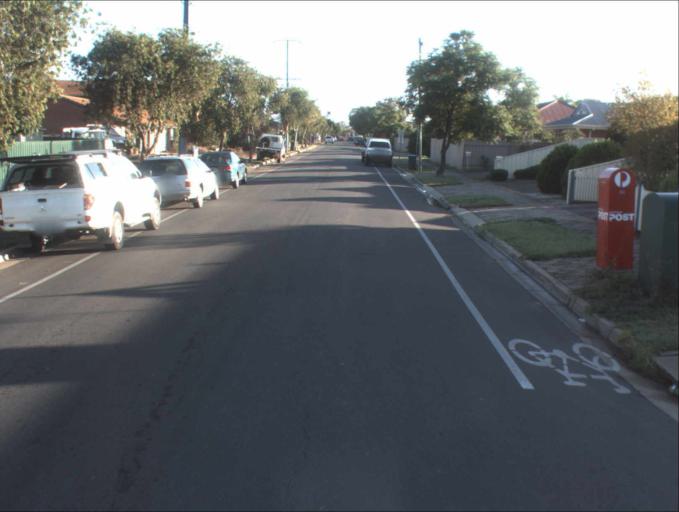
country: AU
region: South Australia
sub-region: Port Adelaide Enfield
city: Klemzig
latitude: -34.8713
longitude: 138.6438
